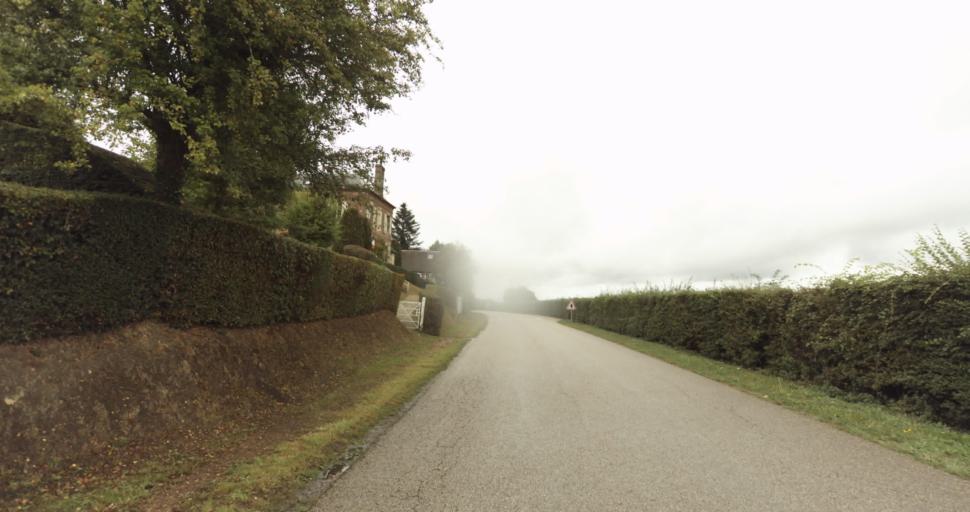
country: FR
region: Lower Normandy
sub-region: Departement de l'Orne
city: Vimoutiers
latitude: 48.9069
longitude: 0.2073
